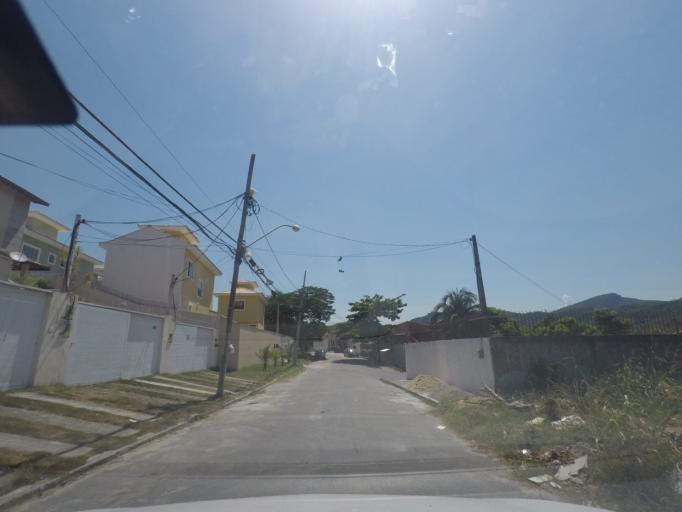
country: BR
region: Rio de Janeiro
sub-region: Niteroi
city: Niteroi
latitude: -22.9329
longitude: -43.0134
